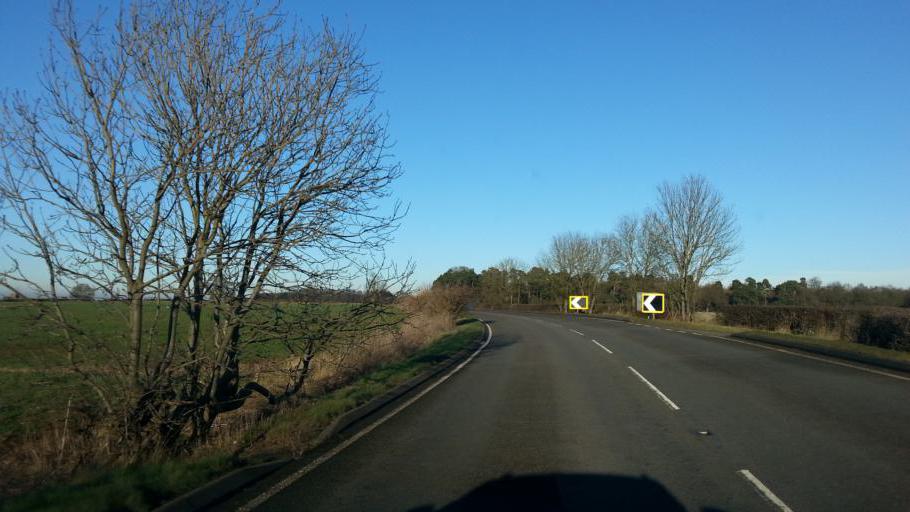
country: GB
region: England
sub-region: Leicestershire
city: Wymondham
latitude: 52.8340
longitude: -0.8042
